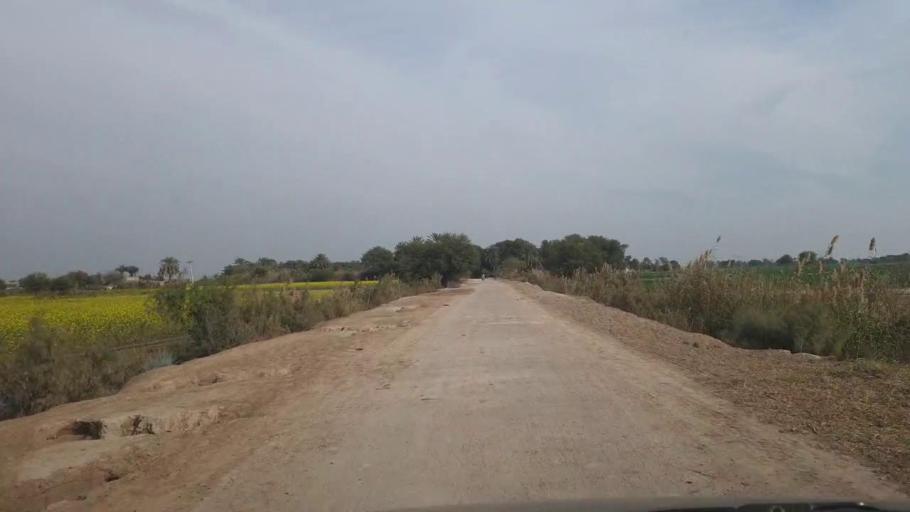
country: PK
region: Sindh
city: Shahpur Chakar
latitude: 26.0798
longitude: 68.4955
